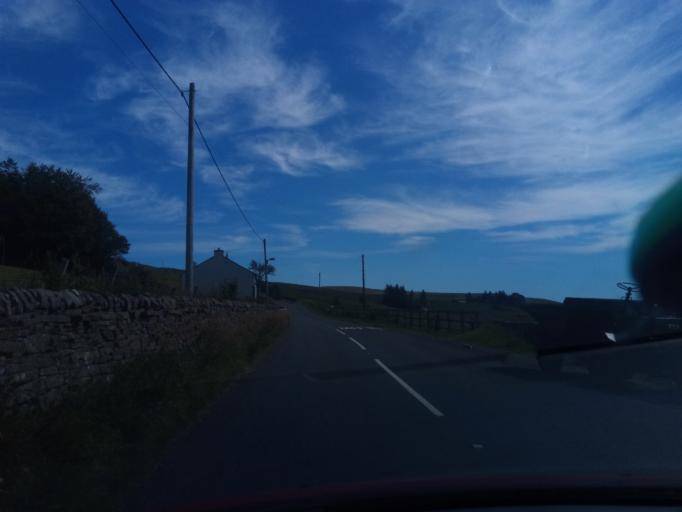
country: GB
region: England
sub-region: County Durham
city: Holwick
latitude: 54.7669
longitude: -2.2402
